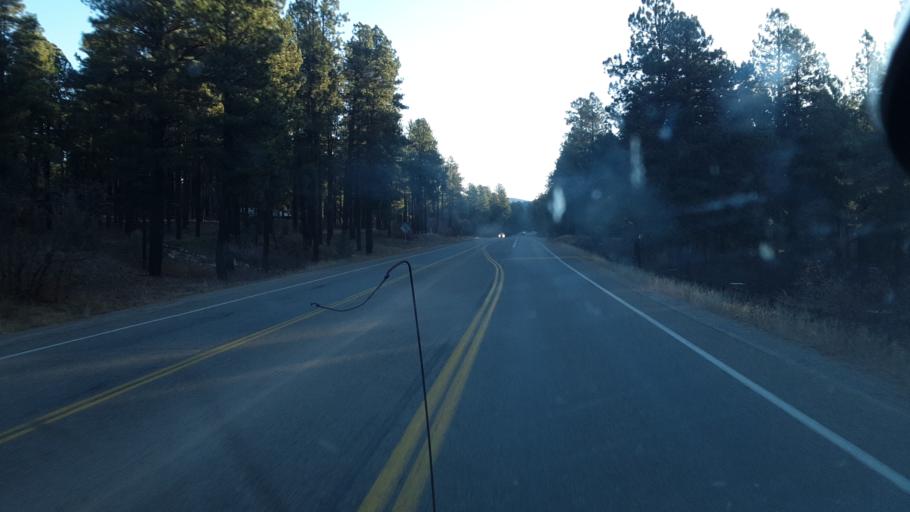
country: US
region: Colorado
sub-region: La Plata County
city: Durango
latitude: 37.3113
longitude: -107.7955
